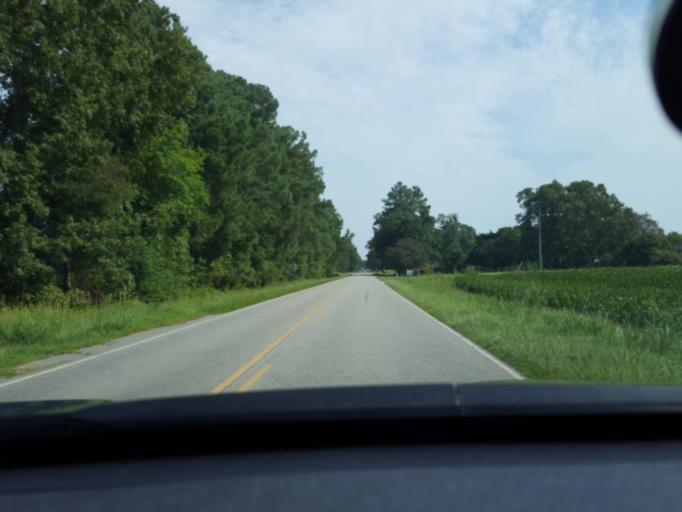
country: US
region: North Carolina
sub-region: Washington County
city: Plymouth
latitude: 35.8821
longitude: -76.7100
